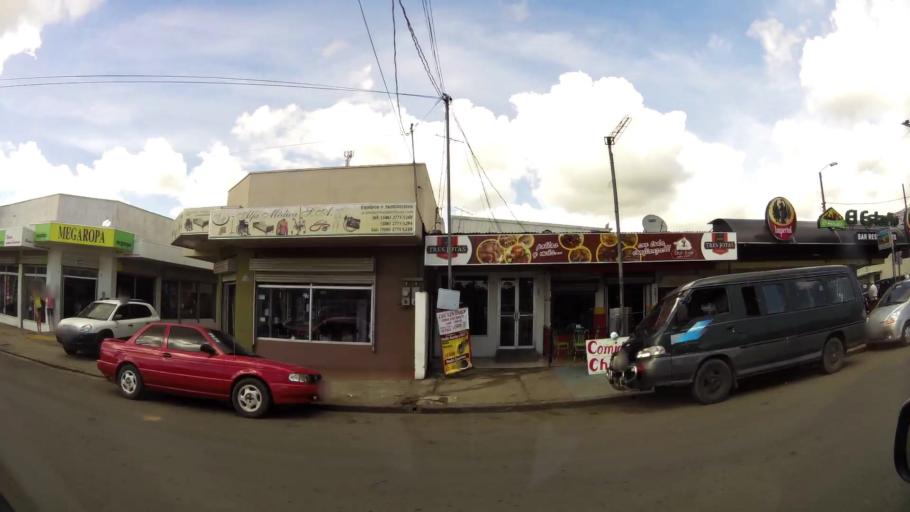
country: CR
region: San Jose
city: San Isidro
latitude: 9.3693
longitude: -83.7052
